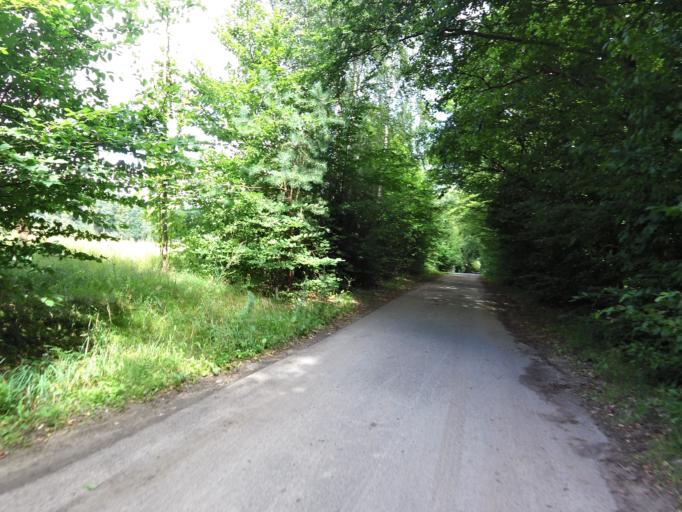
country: DE
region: Brandenburg
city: Lychen
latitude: 53.2420
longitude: 13.3630
